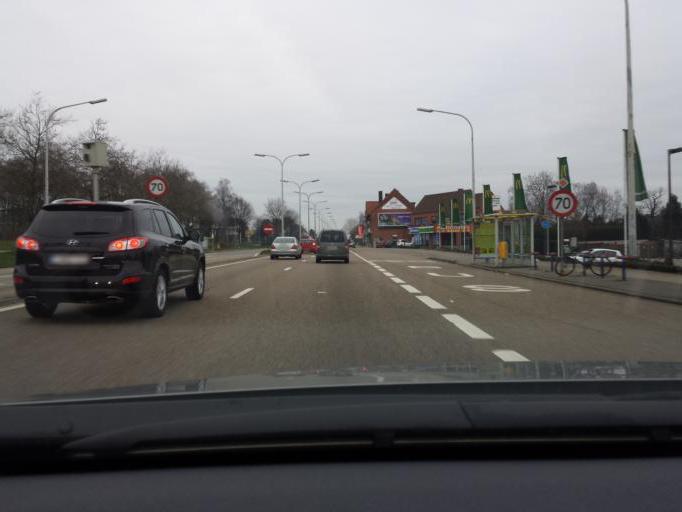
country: BE
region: Flanders
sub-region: Provincie Limburg
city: Houthalen
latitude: 51.0243
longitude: 5.3748
